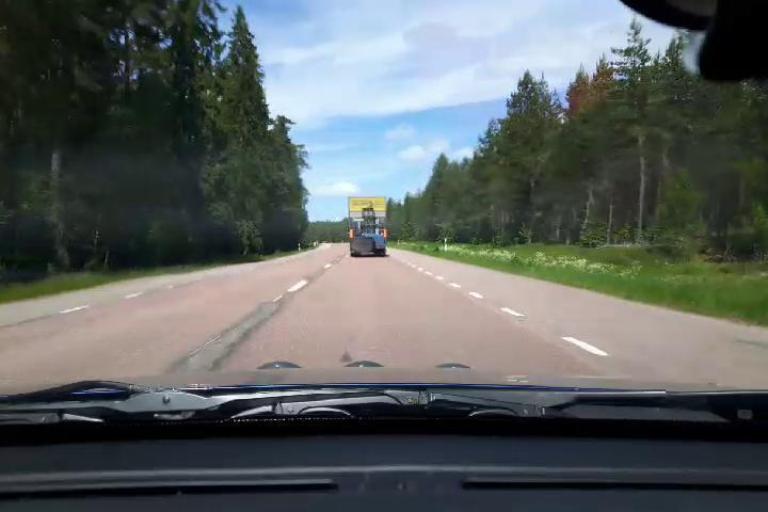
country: SE
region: Uppsala
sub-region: Osthammars Kommun
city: Bjorklinge
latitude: 60.1274
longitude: 17.5095
